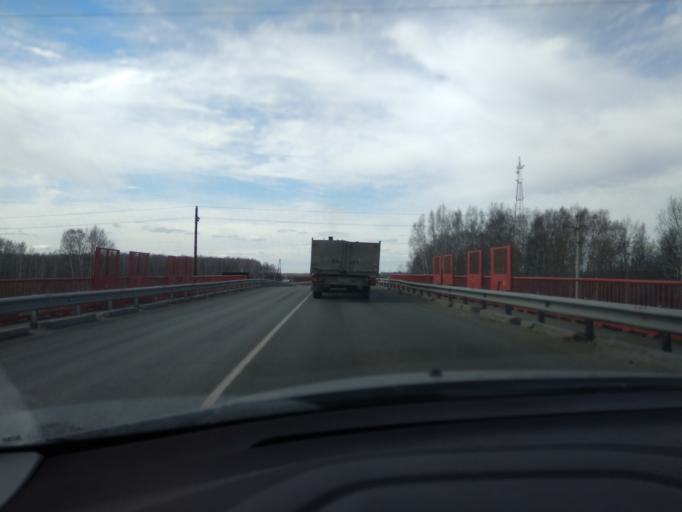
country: RU
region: Sverdlovsk
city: Pyshma
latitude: 56.9566
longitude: 63.2343
